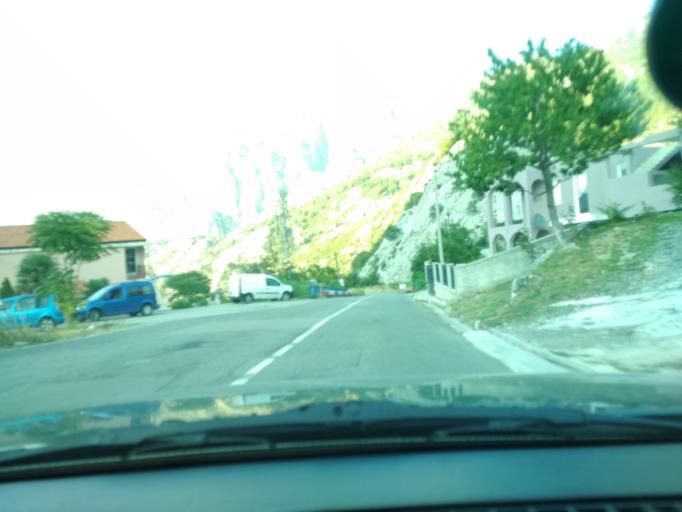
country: ME
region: Kotor
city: Kotor
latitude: 42.4071
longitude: 18.7673
